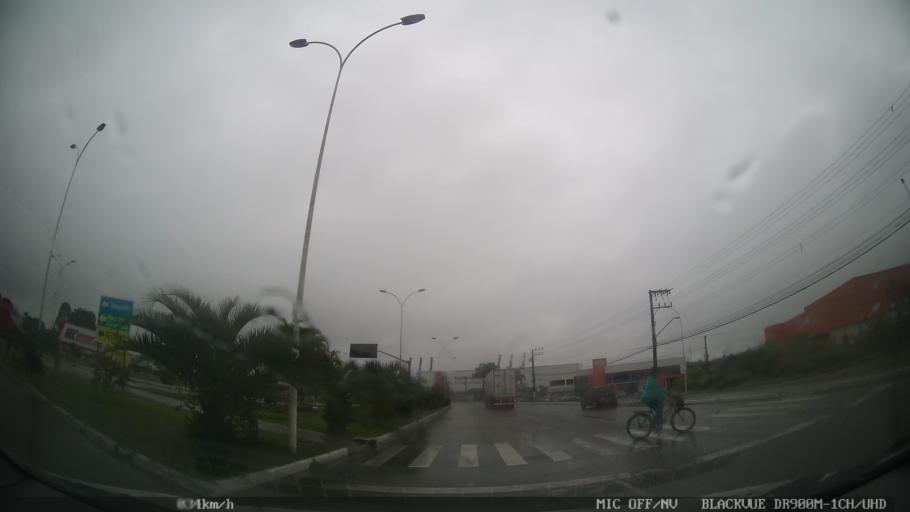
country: BR
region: Santa Catarina
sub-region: Navegantes
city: Navegantes
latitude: -26.8901
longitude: -48.6620
